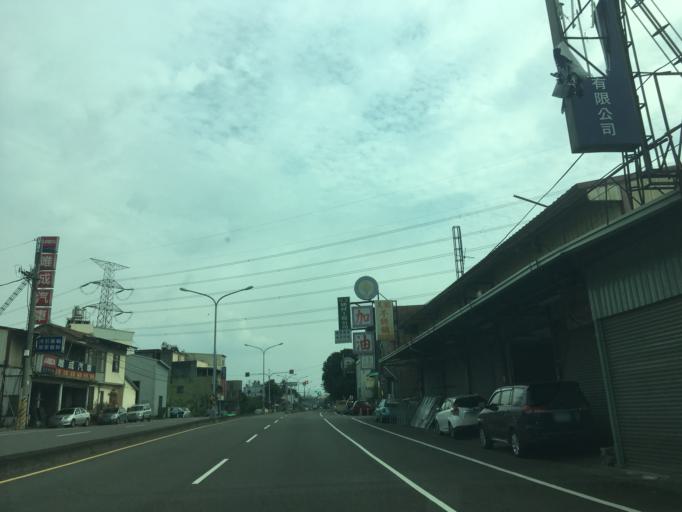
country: TW
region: Taiwan
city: Zhongxing New Village
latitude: 24.0210
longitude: 120.6963
